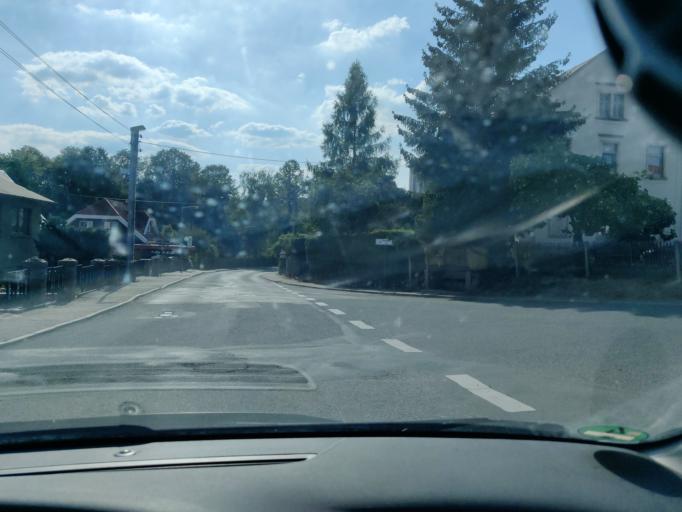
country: DE
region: Saxony
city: Mittweida
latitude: 50.9909
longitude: 12.9893
